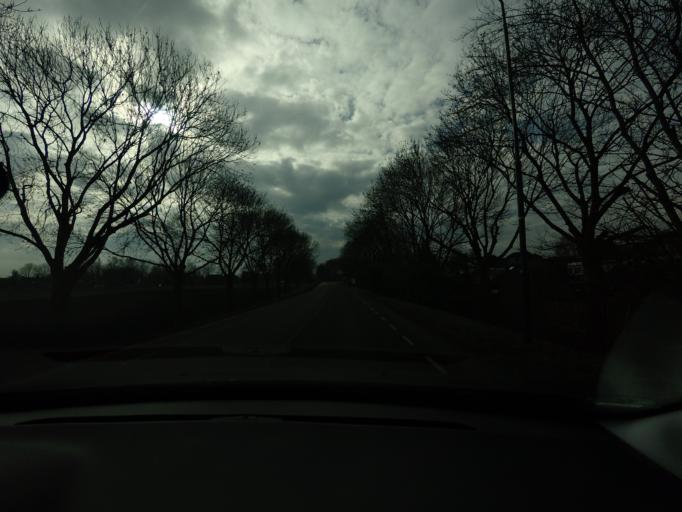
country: NL
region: North Brabant
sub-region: Gemeente Waalwijk
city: Waspik
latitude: 51.6910
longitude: 4.9483
